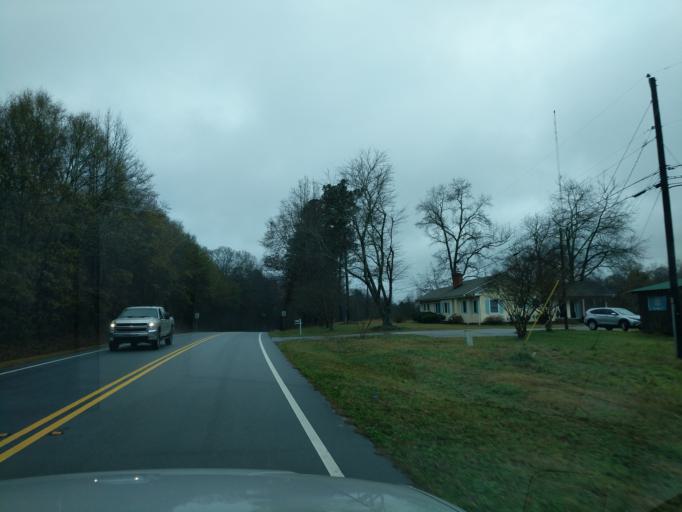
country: US
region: Georgia
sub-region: Franklin County
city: Lavonia
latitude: 34.3698
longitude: -83.0868
